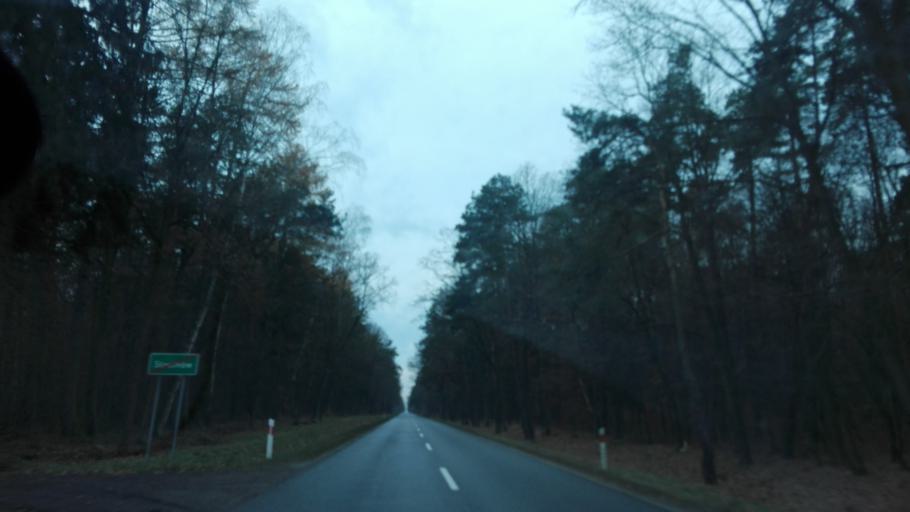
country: PL
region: Lublin Voivodeship
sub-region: Powiat radzynski
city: Radzyn Podlaski
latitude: 51.7787
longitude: 22.6901
